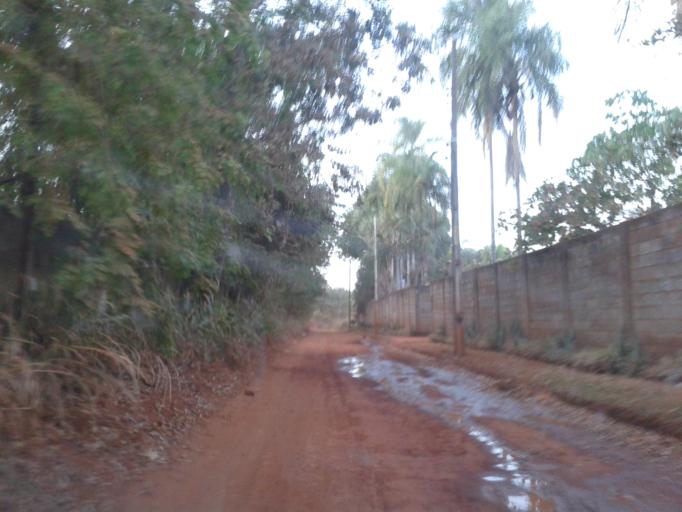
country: BR
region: Goias
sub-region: Goiania
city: Goiania
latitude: -16.6470
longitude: -49.3529
